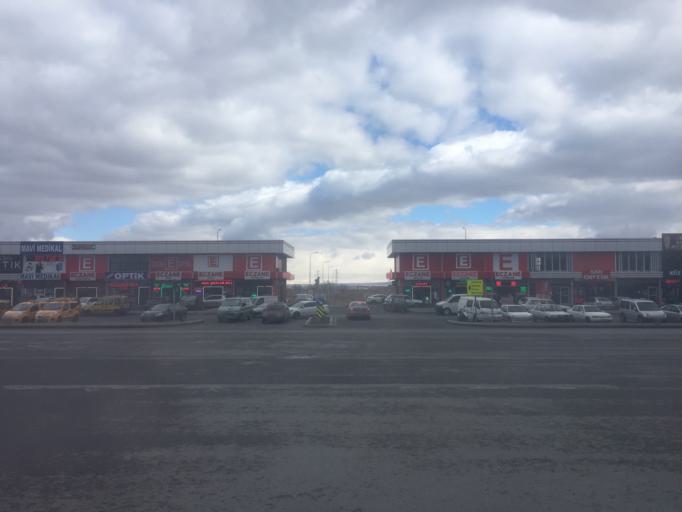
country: TR
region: Kayseri
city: Melikgazi
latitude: 38.7702
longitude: 35.4126
